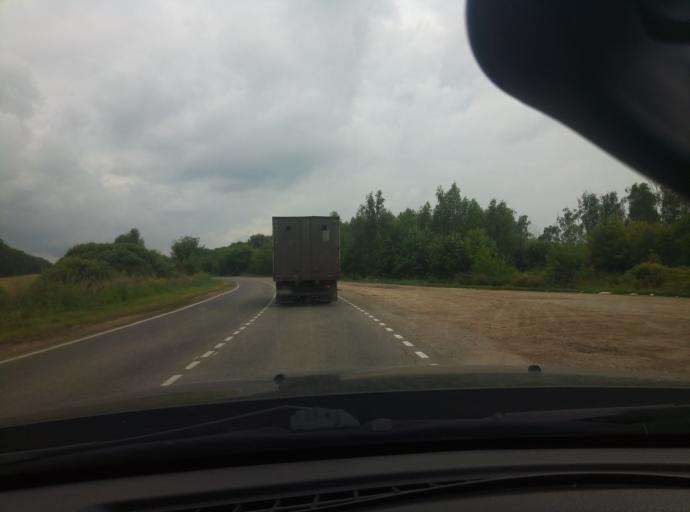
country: RU
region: Tula
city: Kimovsk
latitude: 53.9492
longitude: 38.5326
